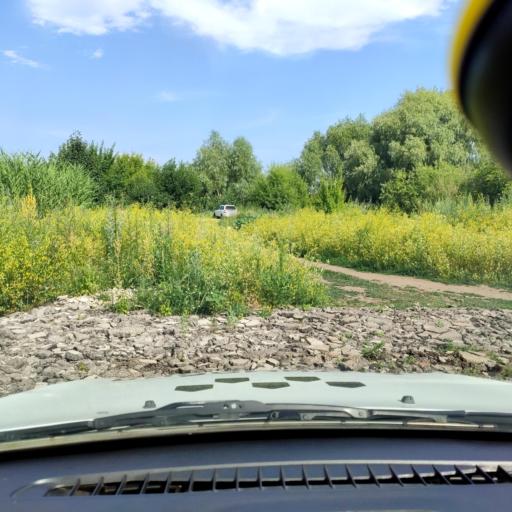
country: RU
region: Samara
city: Podstepki
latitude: 53.5028
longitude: 49.1441
